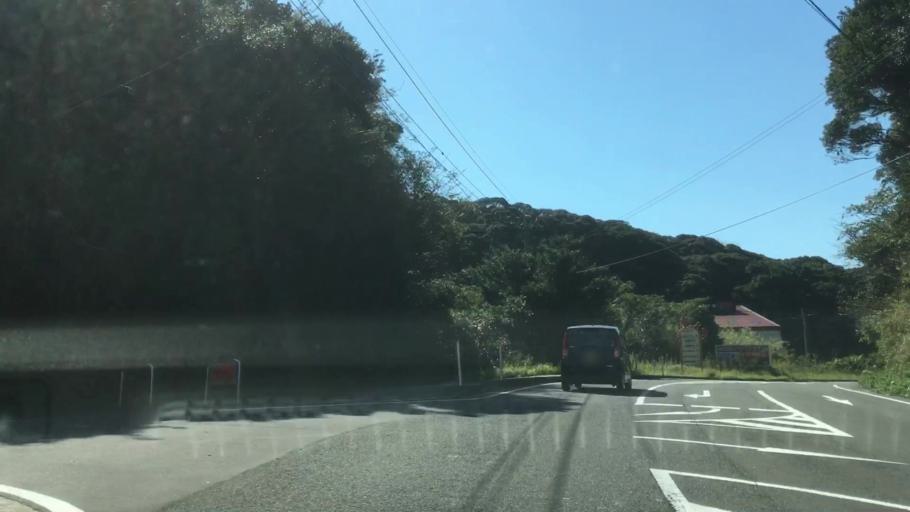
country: JP
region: Nagasaki
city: Sasebo
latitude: 33.0254
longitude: 129.5776
